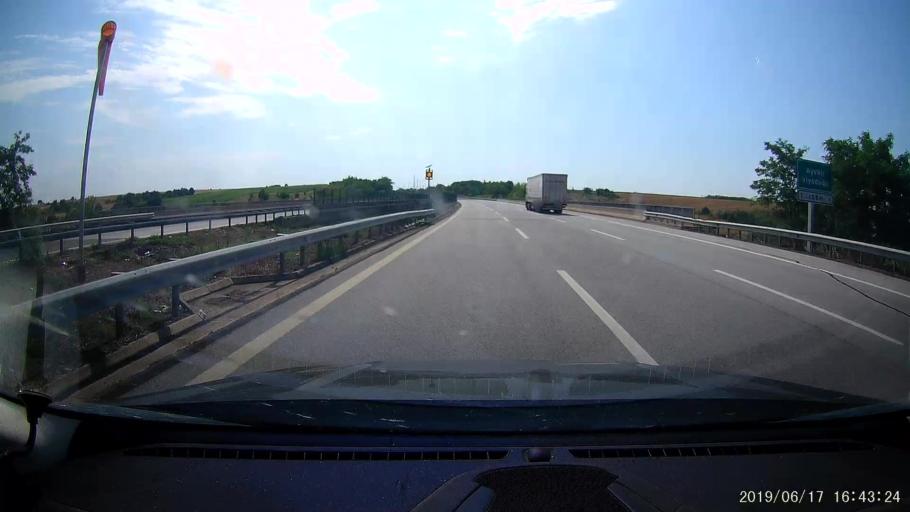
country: TR
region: Kirklareli
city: Luleburgaz
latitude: 41.4808
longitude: 27.2944
